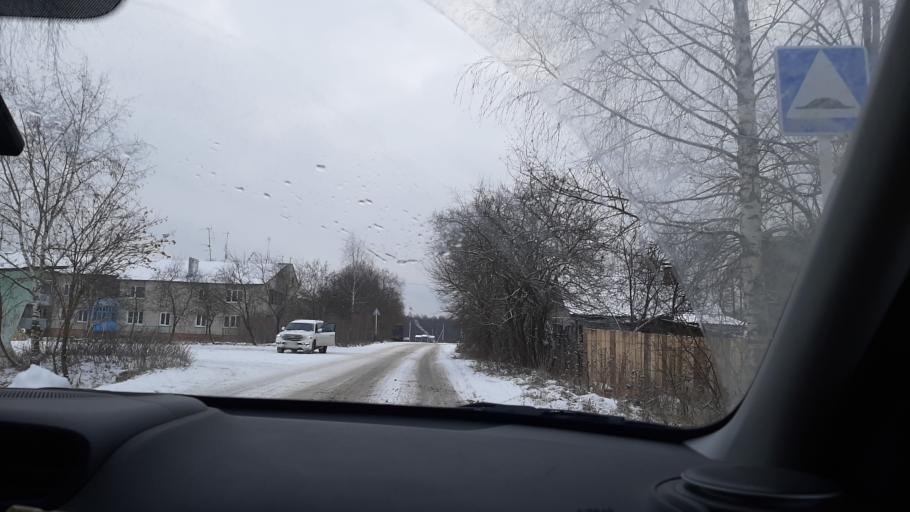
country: RU
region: Ivanovo
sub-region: Gorod Ivanovo
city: Ivanovo
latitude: 56.9271
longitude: 40.9823
